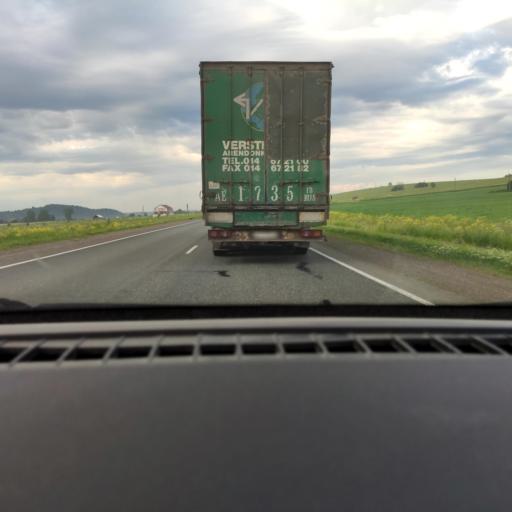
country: RU
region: Perm
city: Chastyye
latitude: 57.3853
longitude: 54.4379
